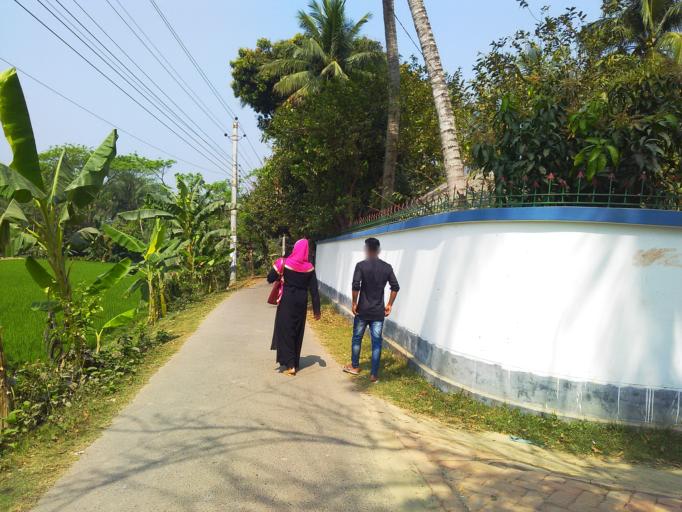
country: BD
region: Khulna
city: Khulna
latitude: 22.8779
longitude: 89.5414
